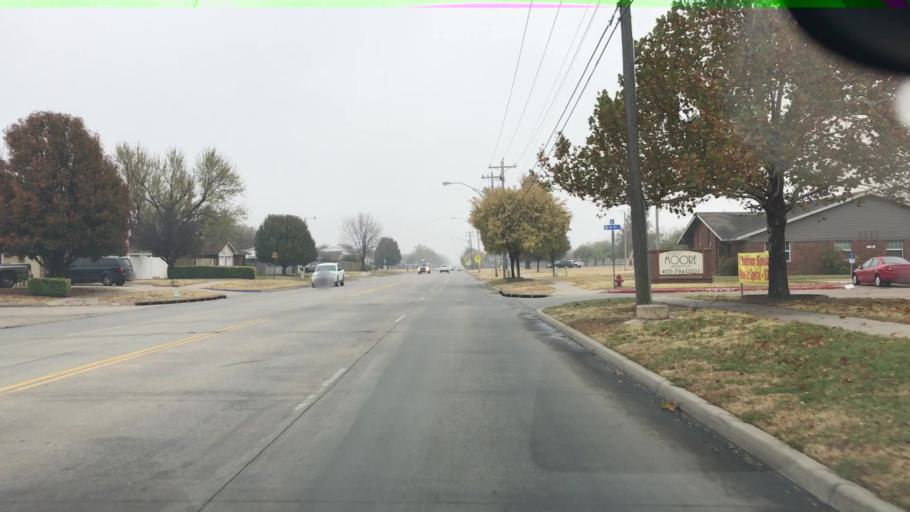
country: US
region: Oklahoma
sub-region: Cleveland County
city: Moore
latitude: 35.3472
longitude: -97.5122
